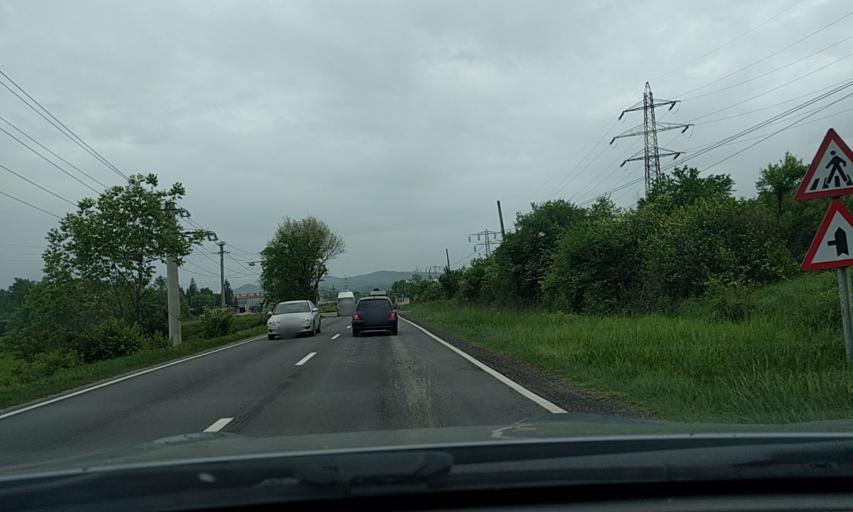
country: RO
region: Dambovita
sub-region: Comuna Vulcana-Pandele
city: Vulcana-Pandele
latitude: 45.0018
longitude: 25.4016
